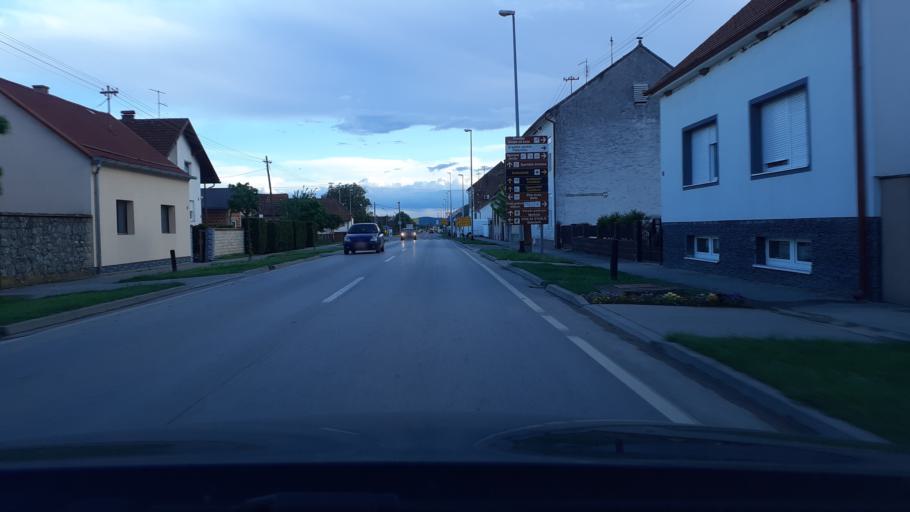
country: HR
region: Pozesko-Slavonska
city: Pleternica
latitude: 45.2911
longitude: 17.8069
